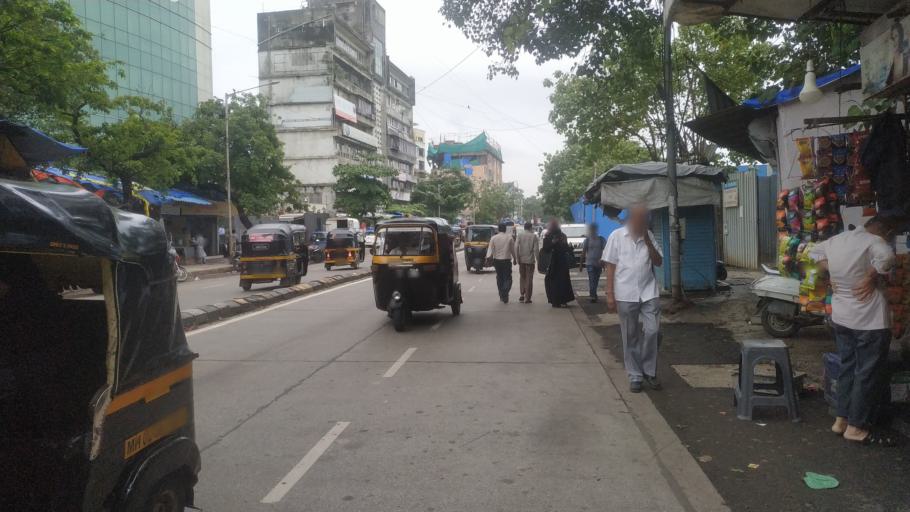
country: IN
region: Maharashtra
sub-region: Mumbai Suburban
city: Mumbai
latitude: 19.0582
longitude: 72.8380
